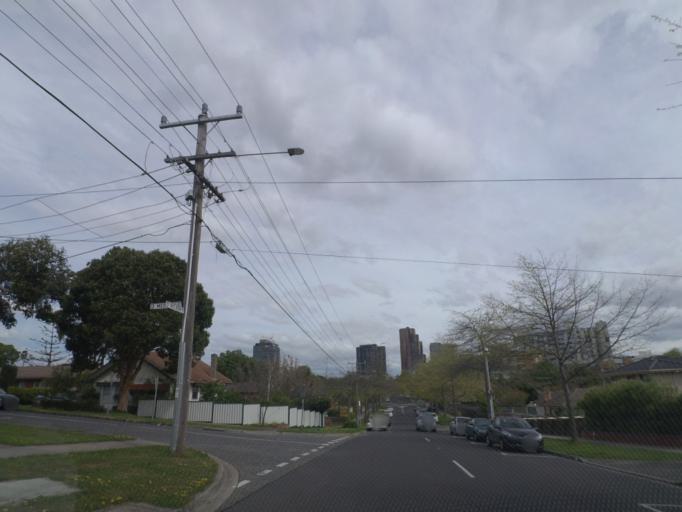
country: AU
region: Victoria
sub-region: Whitehorse
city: Box Hill
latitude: -37.8108
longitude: 145.1205
